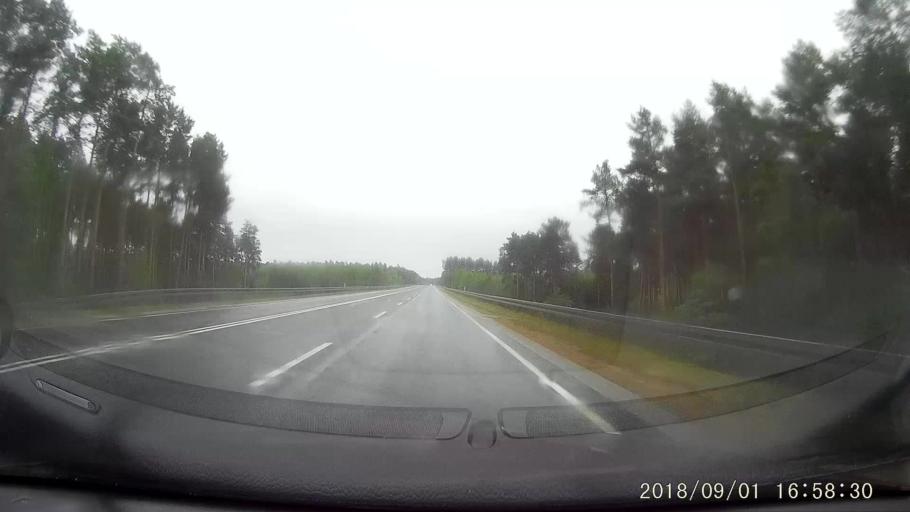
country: PL
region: Lubusz
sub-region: Powiat zielonogorski
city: Swidnica
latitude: 51.9187
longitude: 15.4188
